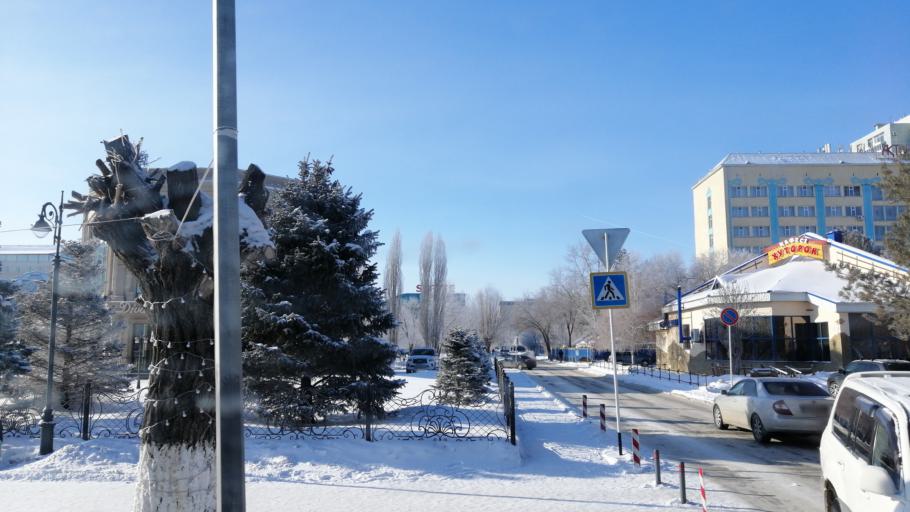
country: KZ
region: Aqtoebe
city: Aqtobe
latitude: 50.2976
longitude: 57.1564
